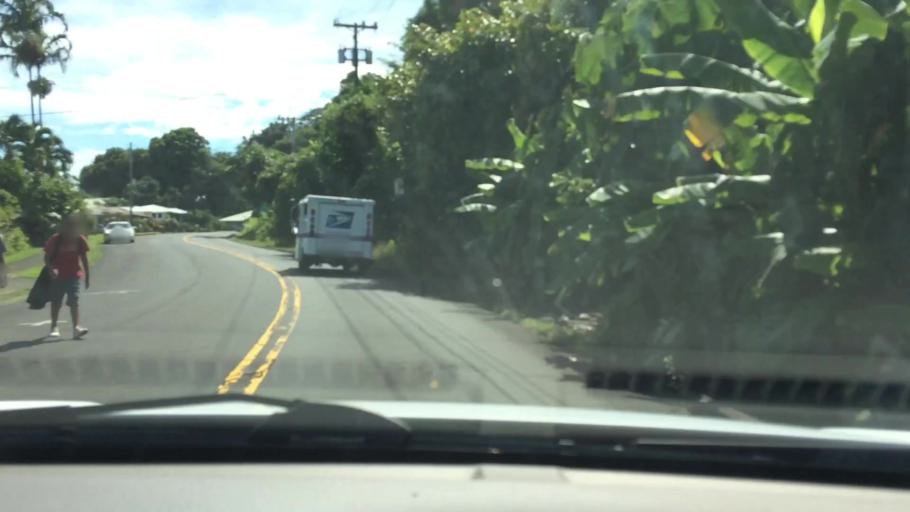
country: US
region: Hawaii
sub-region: Hawaii County
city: Hilo
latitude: 19.7255
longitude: -155.0914
